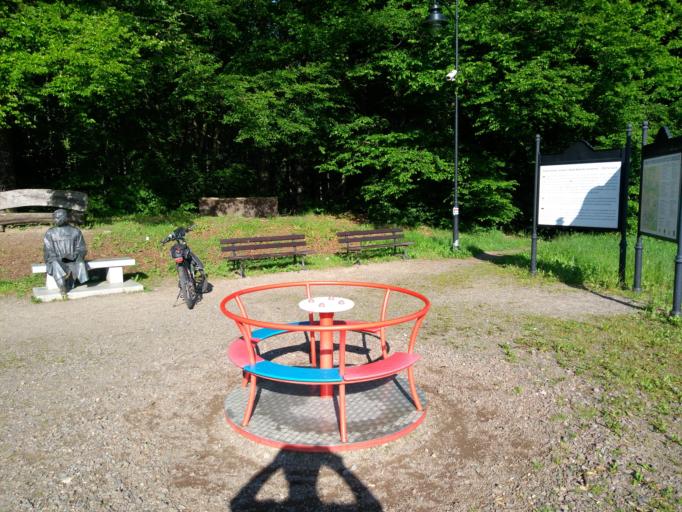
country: PL
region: Pomeranian Voivodeship
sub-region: Powiat kartuski
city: Kartuzy
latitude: 54.3261
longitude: 18.1822
